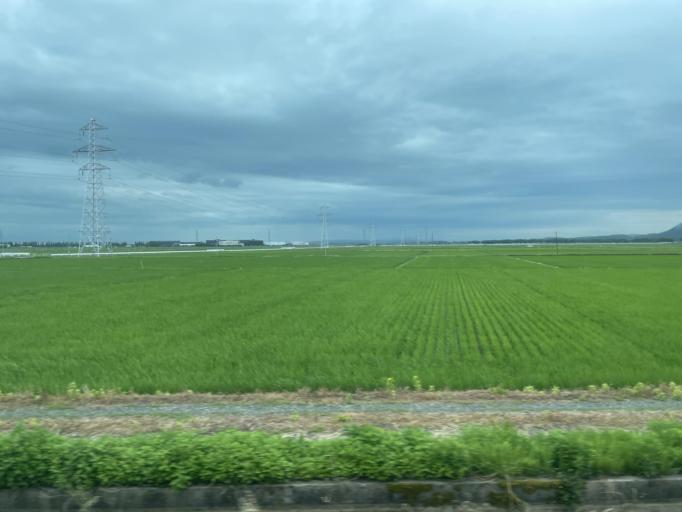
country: JP
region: Niigata
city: Yoshida-kasugacho
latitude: 37.6871
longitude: 138.8603
